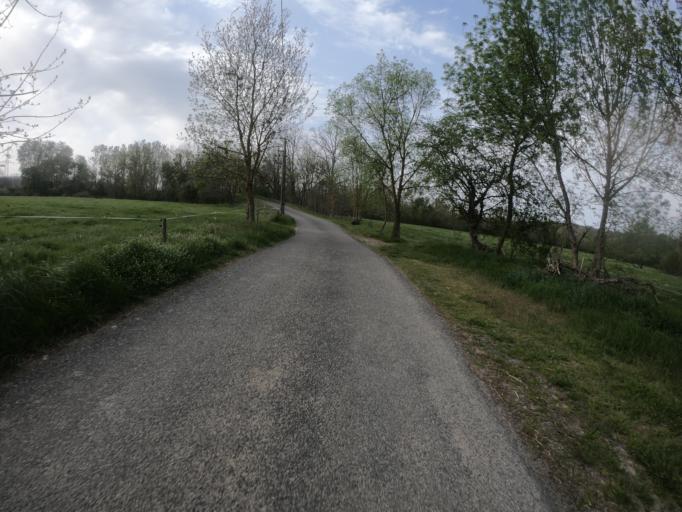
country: FR
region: Languedoc-Roussillon
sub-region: Departement de l'Aude
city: Belpech
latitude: 43.1225
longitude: 1.7385
